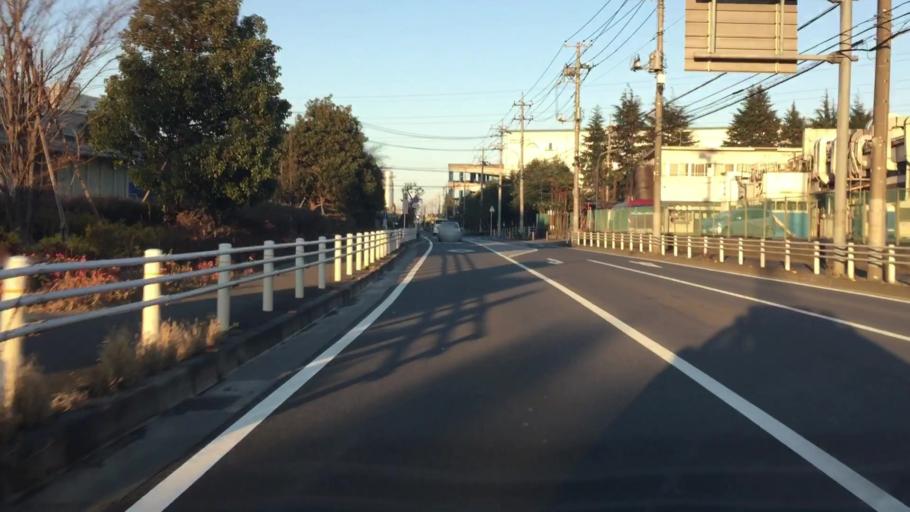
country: JP
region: Chiba
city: Kashiwa
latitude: 35.9066
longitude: 139.9465
